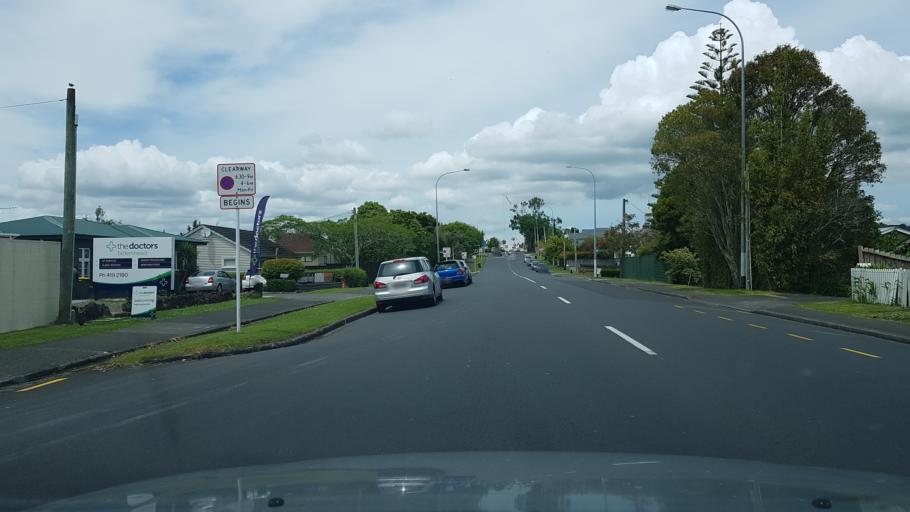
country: NZ
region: Auckland
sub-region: Auckland
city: North Shore
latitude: -36.8070
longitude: 174.7255
